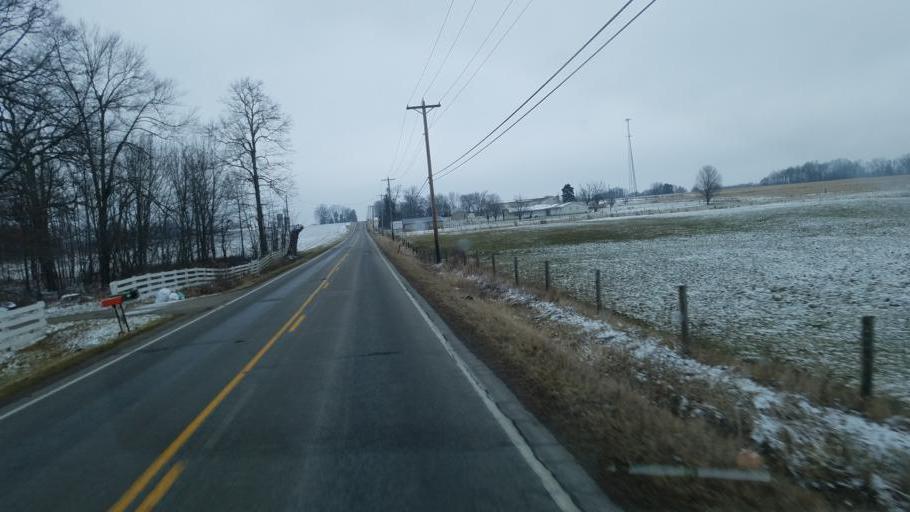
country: US
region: Ohio
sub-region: Wayne County
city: Apple Creek
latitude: 40.7864
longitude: -81.8440
